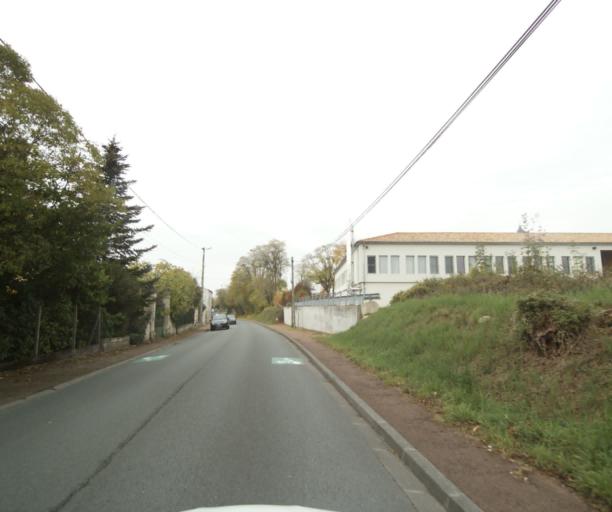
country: FR
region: Poitou-Charentes
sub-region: Departement de la Charente-Maritime
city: Saintes
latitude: 45.7488
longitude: -0.6519
